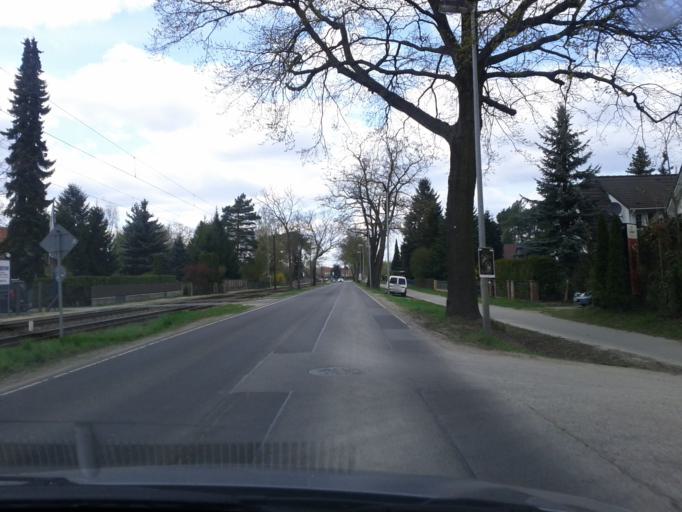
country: DE
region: Brandenburg
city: Schoneiche
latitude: 52.4753
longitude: 13.7116
